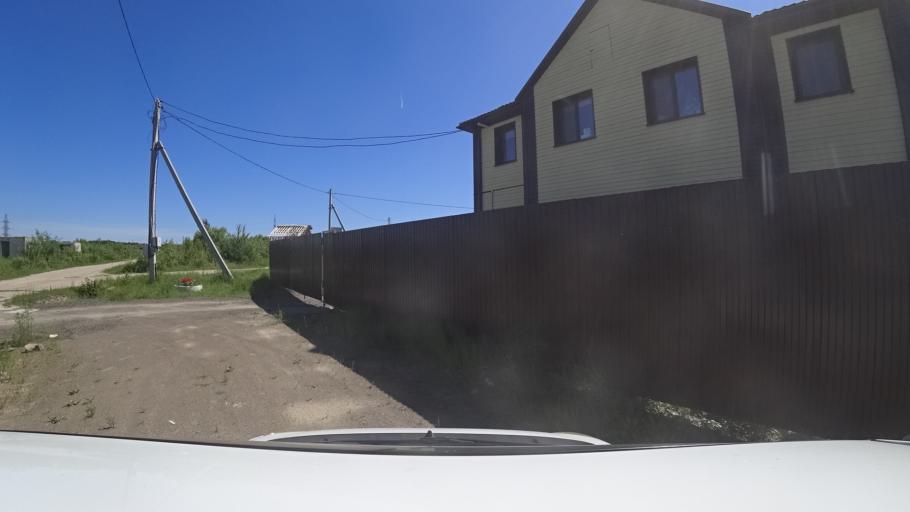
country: RU
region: Khabarovsk Krai
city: Topolevo
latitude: 48.5657
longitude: 135.1923
